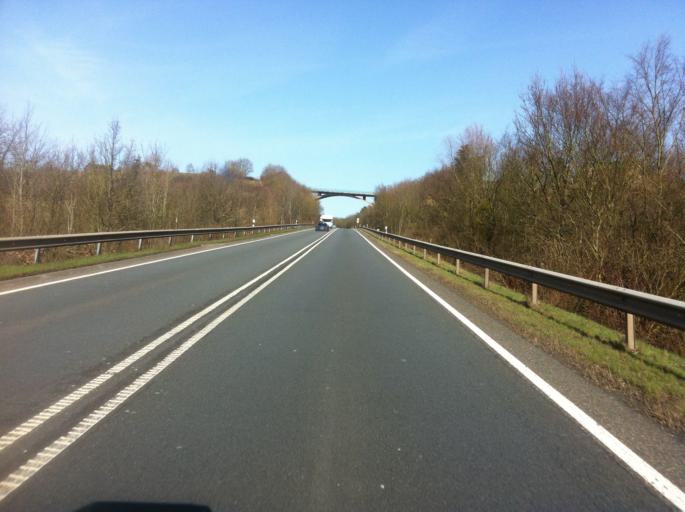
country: DE
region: Rheinland-Pfalz
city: Mendig
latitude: 50.3650
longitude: 7.2696
